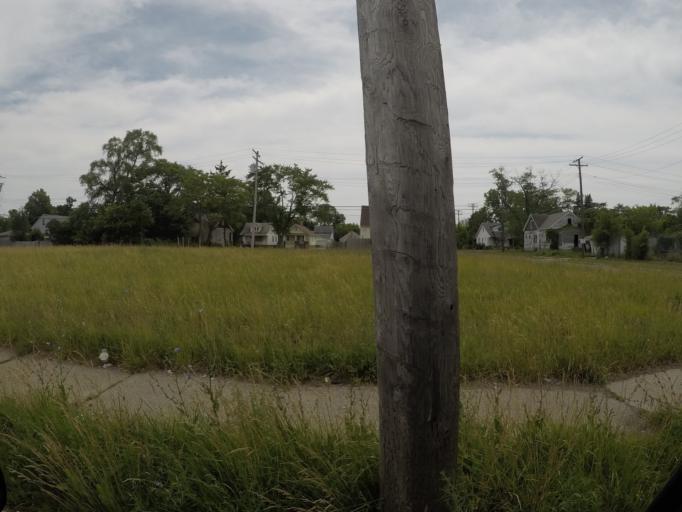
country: US
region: Michigan
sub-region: Macomb County
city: Eastpointe
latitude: 42.4353
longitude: -82.9678
